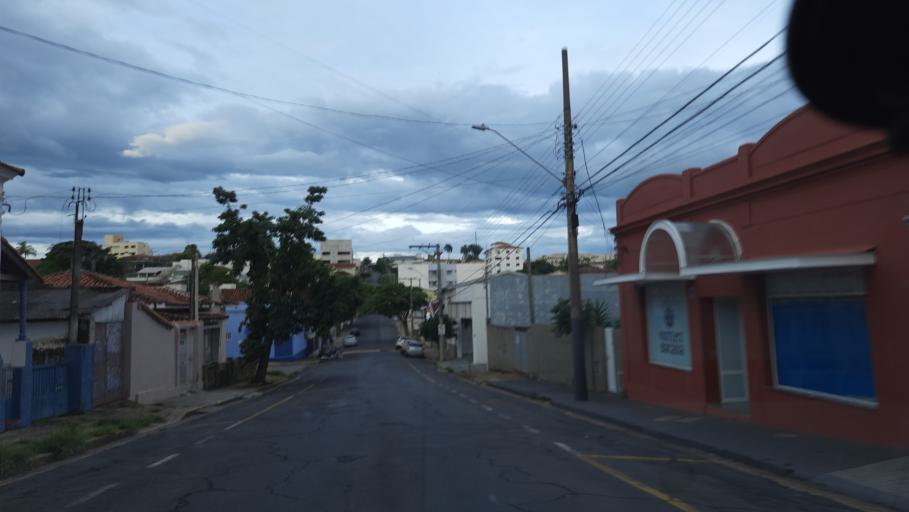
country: BR
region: Sao Paulo
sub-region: Sao Joao Da Boa Vista
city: Sao Joao da Boa Vista
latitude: -21.9676
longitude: -46.7947
